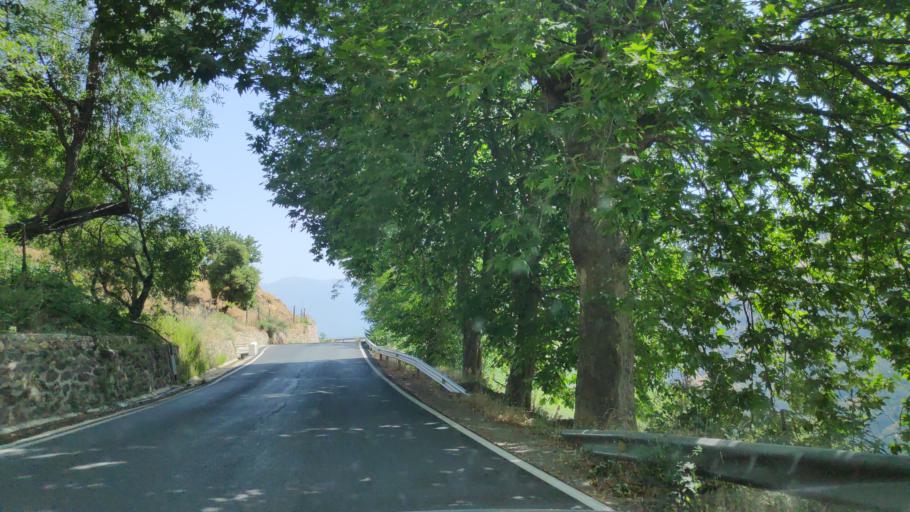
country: ES
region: Andalusia
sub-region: Provincia de Granada
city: Capileira
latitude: 36.9582
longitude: -3.3567
